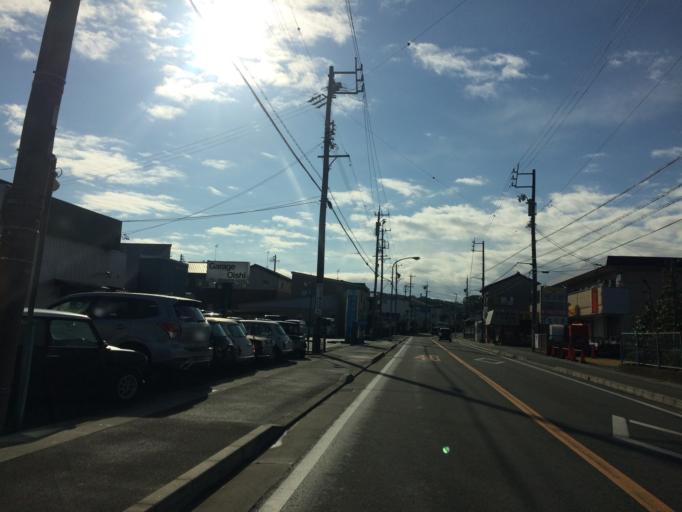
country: JP
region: Shizuoka
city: Shizuoka-shi
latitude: 34.9858
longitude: 138.4259
